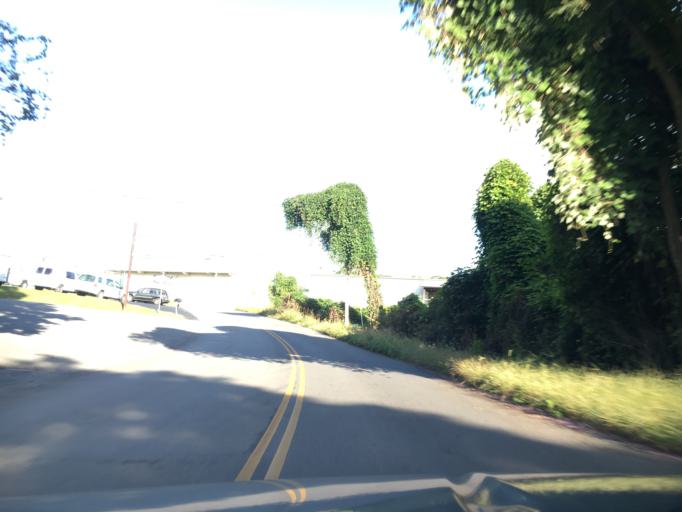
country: US
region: Virginia
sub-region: City of Lynchburg
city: West Lynchburg
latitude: 37.3881
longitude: -79.1596
